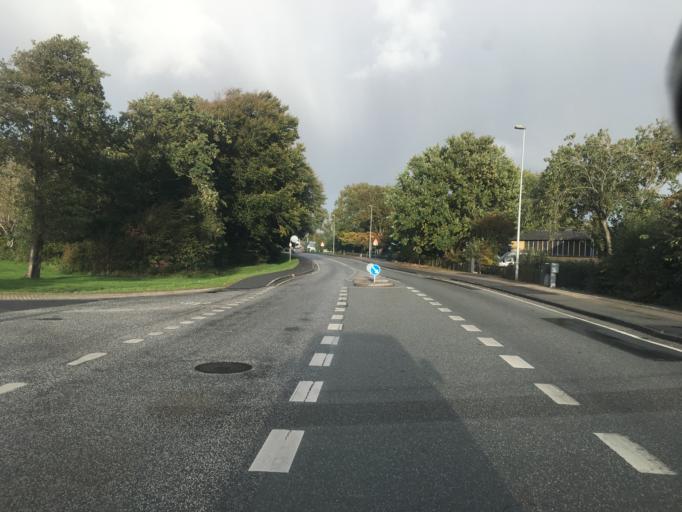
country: DK
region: South Denmark
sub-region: Tonder Kommune
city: Tonder
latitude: 54.9480
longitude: 8.8808
